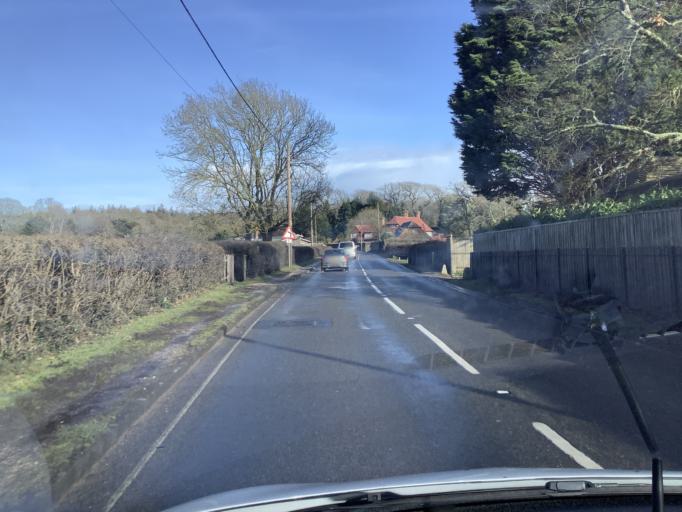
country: GB
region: England
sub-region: Hampshire
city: Hythe
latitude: 50.8203
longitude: -1.4479
